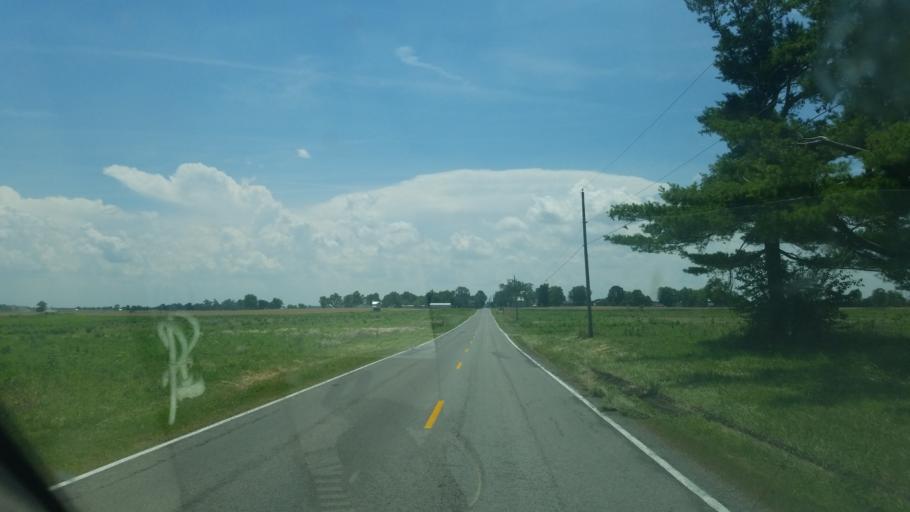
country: US
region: Ohio
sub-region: Hancock County
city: Arlington
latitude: 40.9420
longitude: -83.5944
